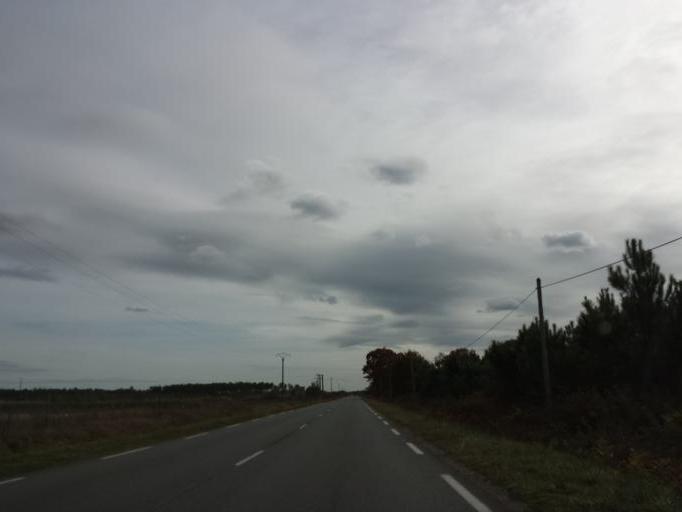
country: FR
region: Aquitaine
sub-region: Departement de la Gironde
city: Marcheprime
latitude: 44.7671
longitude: -0.9244
